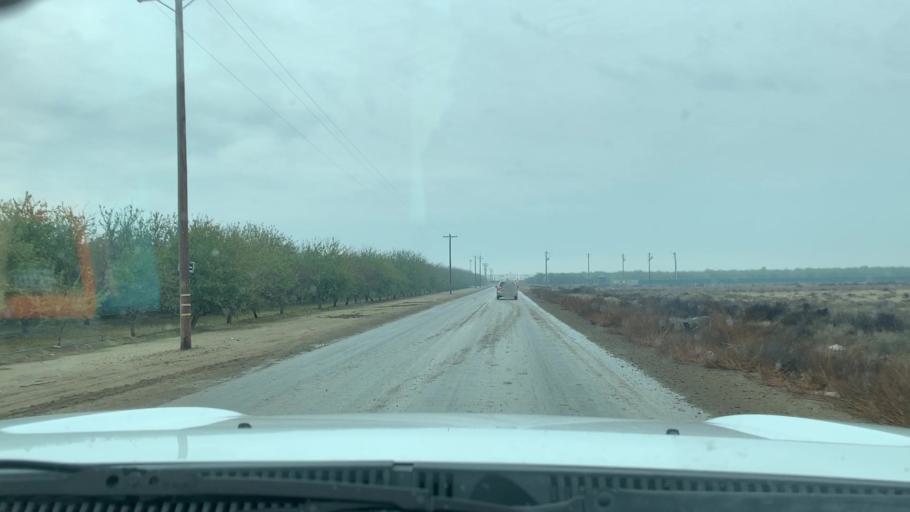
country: US
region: California
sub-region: Kern County
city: Delano
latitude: 35.7612
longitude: -119.3518
